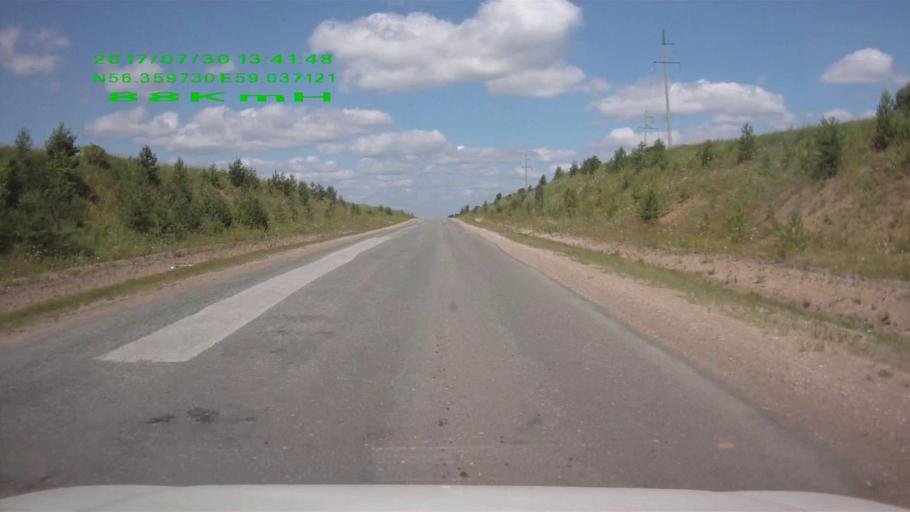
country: RU
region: Sverdlovsk
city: Mikhaylovsk
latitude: 56.3602
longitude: 59.0372
